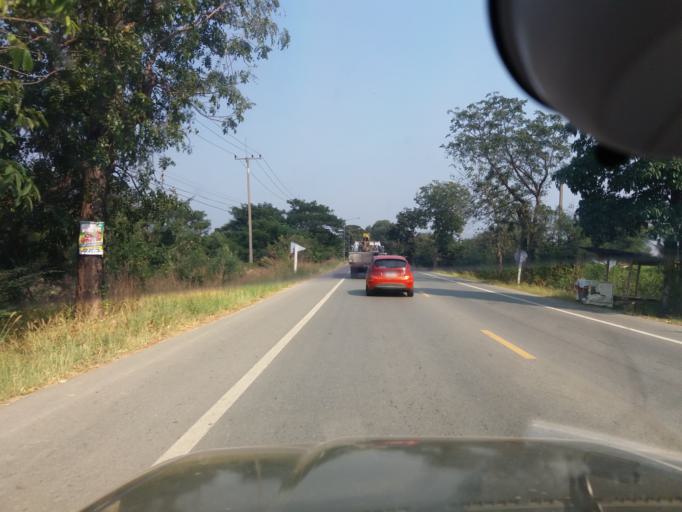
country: TH
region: Sing Buri
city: Bang Racham
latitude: 14.8820
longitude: 100.3584
